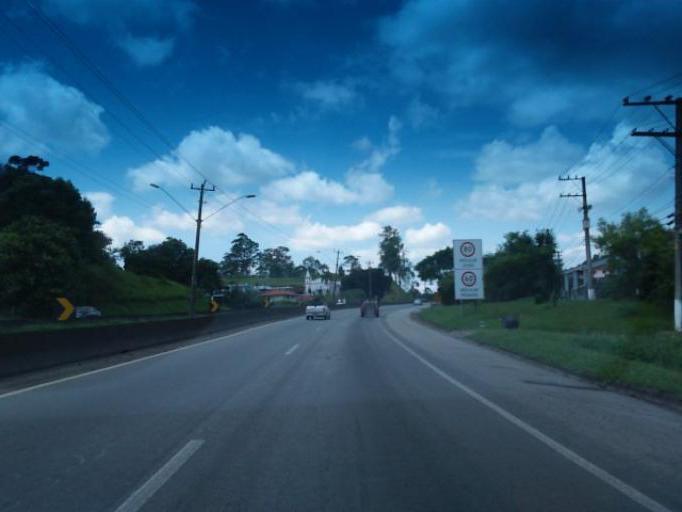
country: BR
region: Sao Paulo
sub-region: Itapecerica Da Serra
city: Itapecerica da Serra
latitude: -23.7394
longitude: -46.8973
